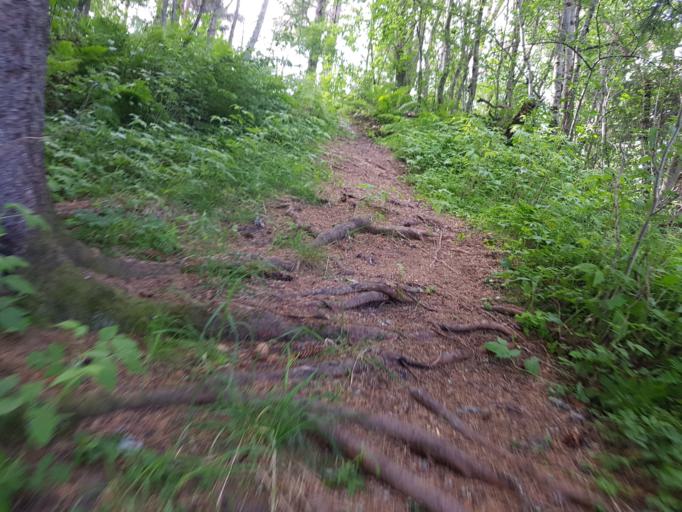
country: NO
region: Sor-Trondelag
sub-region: Trondheim
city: Trondheim
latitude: 63.4042
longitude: 10.3503
